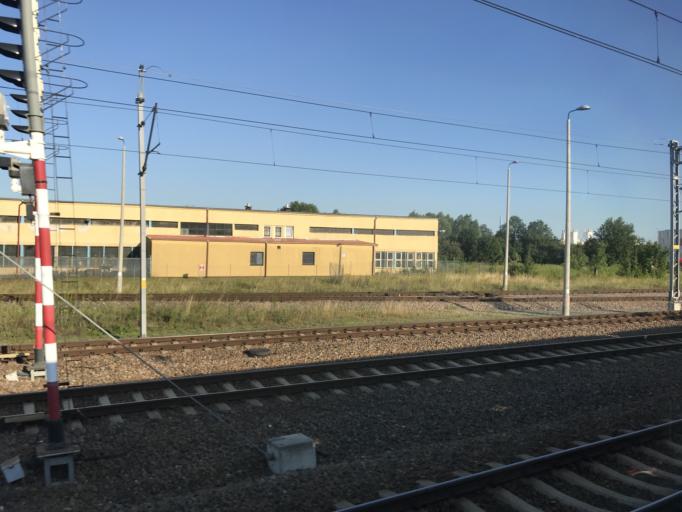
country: PL
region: Pomeranian Voivodeship
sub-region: Gdansk
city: Gdansk
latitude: 54.3333
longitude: 18.6384
